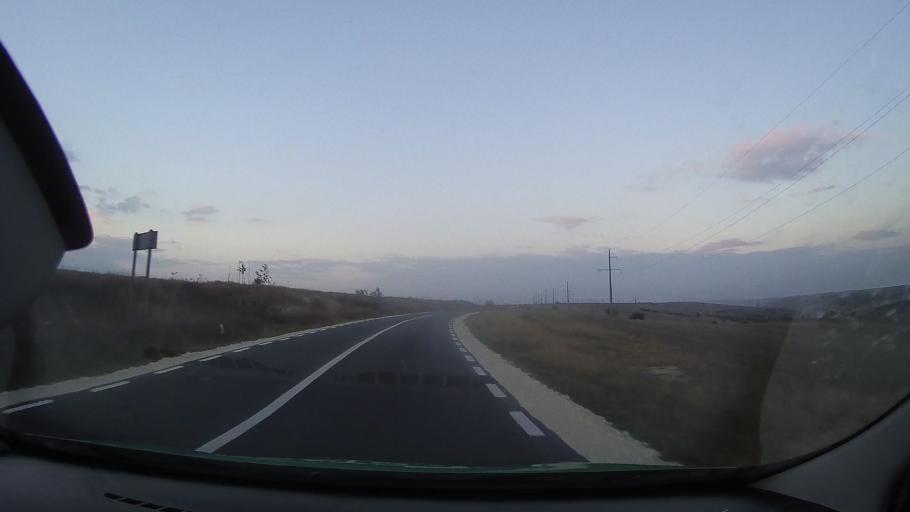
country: RO
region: Constanta
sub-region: Comuna Baneasa
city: Baneasa
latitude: 44.0811
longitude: 27.6892
